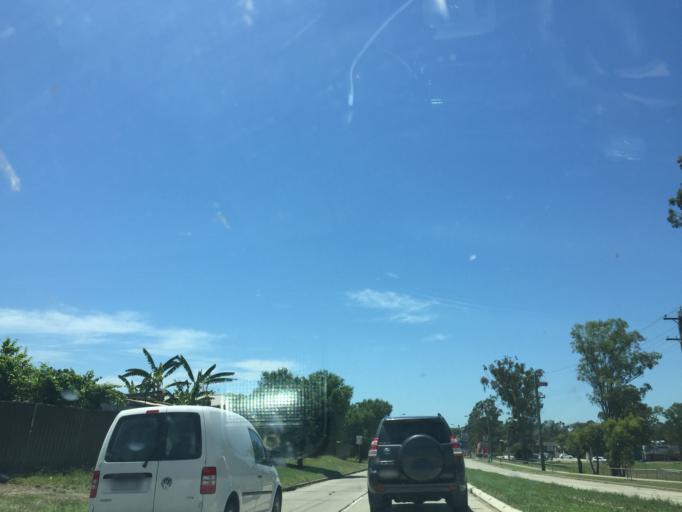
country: AU
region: New South Wales
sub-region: Blacktown
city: Glendenning
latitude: -33.7389
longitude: 150.8584
